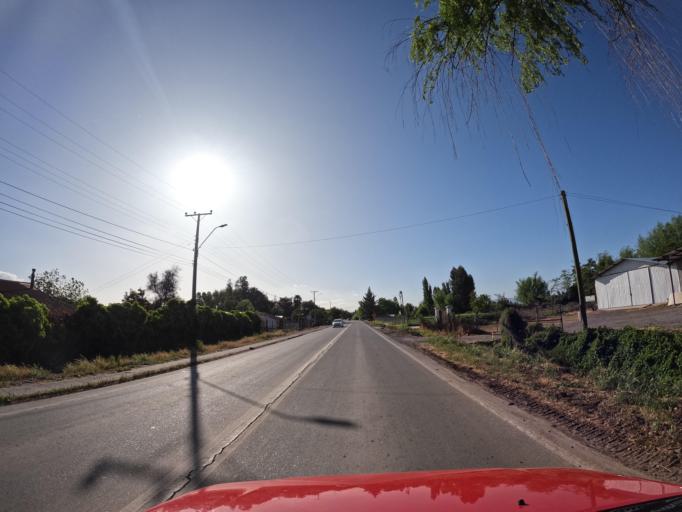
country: CL
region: Maule
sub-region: Provincia de Curico
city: Teno
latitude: -34.7416
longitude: -71.2487
